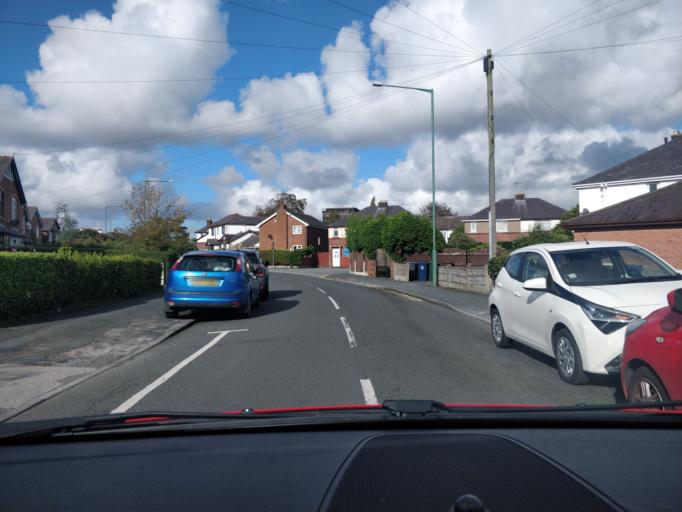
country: GB
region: England
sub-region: Lancashire
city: Ormskirk
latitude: 53.5677
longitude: -2.8724
